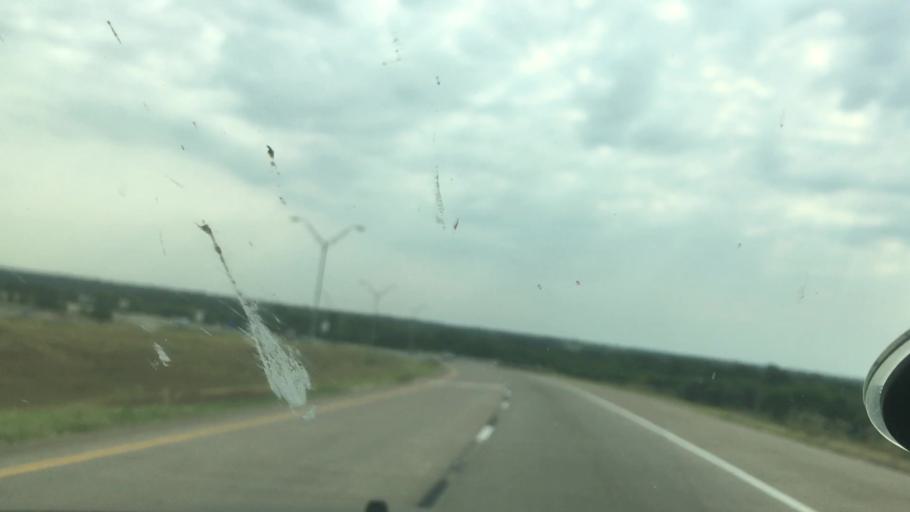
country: US
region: Texas
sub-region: Grayson County
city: Denison
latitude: 33.8005
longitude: -96.5398
